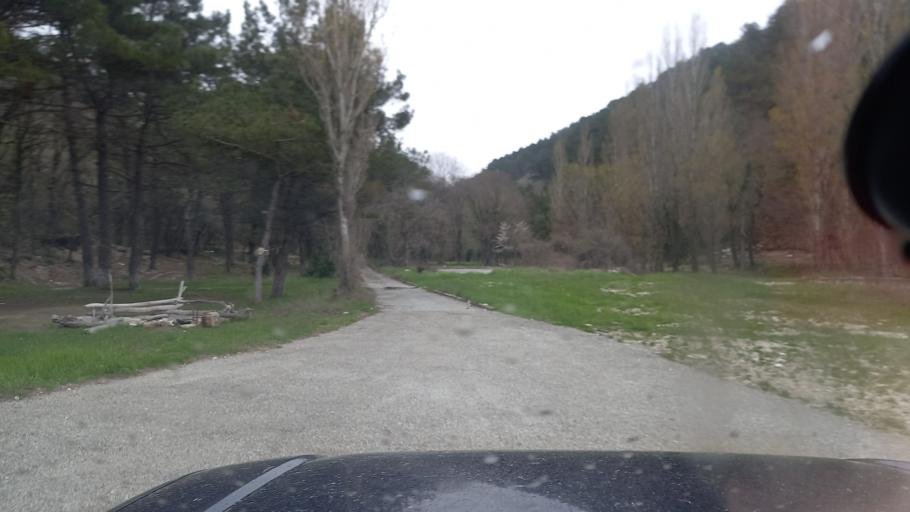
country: RU
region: Krasnodarskiy
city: Arkhipo-Osipovka
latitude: 44.3691
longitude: 38.4492
